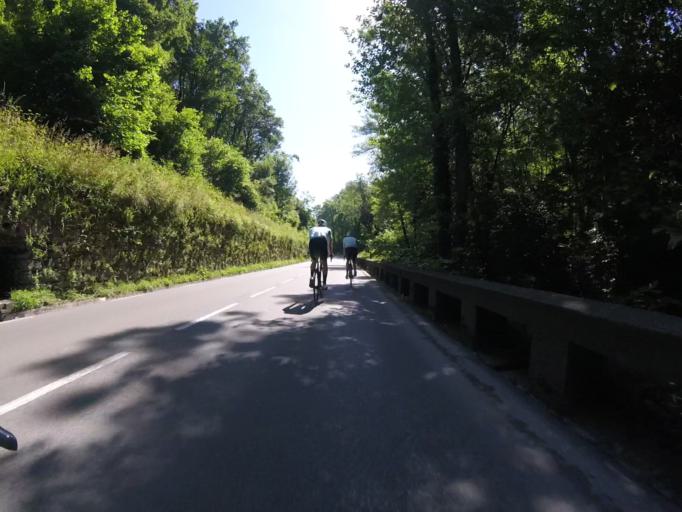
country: ES
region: Basque Country
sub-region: Provincia de Guipuzcoa
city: Alegria de Oria
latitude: 43.1231
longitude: -2.1006
